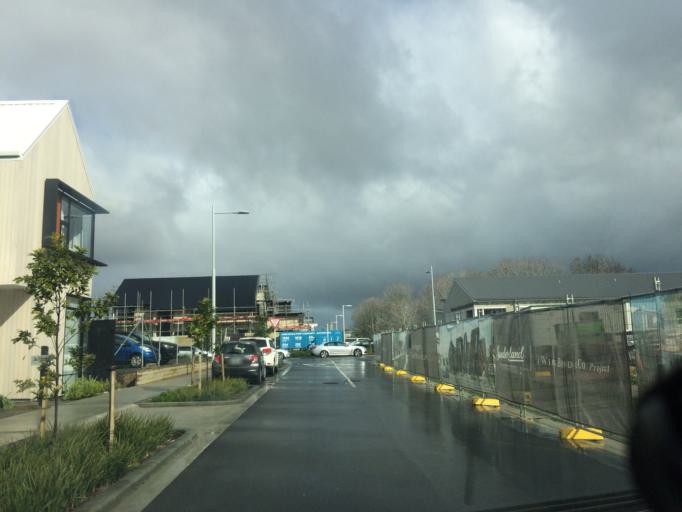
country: NZ
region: Auckland
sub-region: Auckland
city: Rosebank
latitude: -36.7902
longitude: 174.6618
